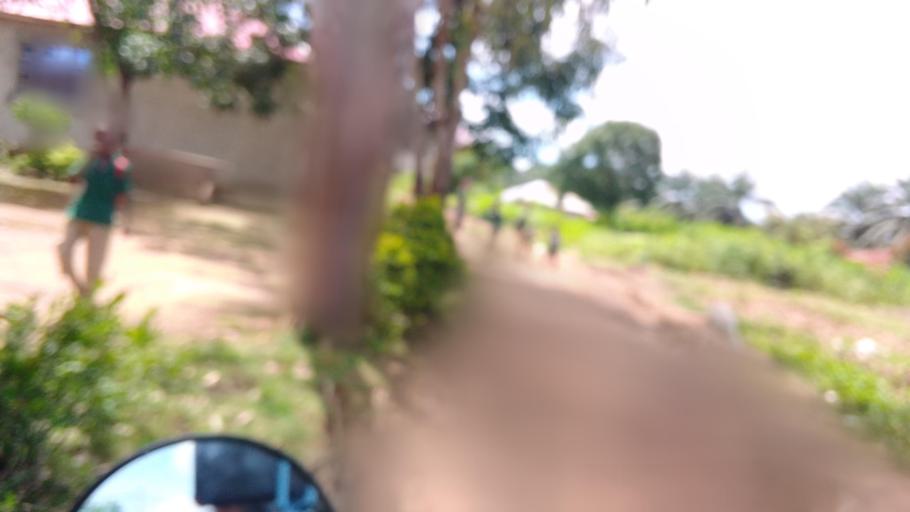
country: SL
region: Northern Province
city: Makeni
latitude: 8.8829
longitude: -12.0273
